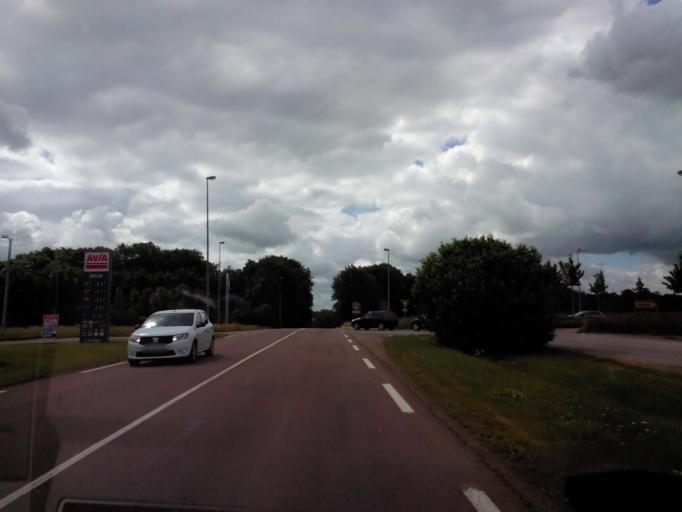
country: FR
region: Bourgogne
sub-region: Departement de la Cote-d'Or
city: Chatillon-sur-Seine
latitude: 47.8763
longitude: 4.5682
